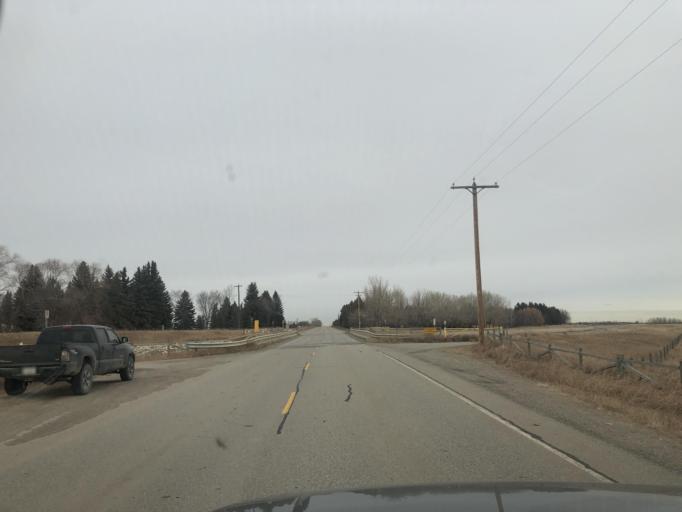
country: CA
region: Alberta
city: Chestermere
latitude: 50.9883
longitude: -113.8654
